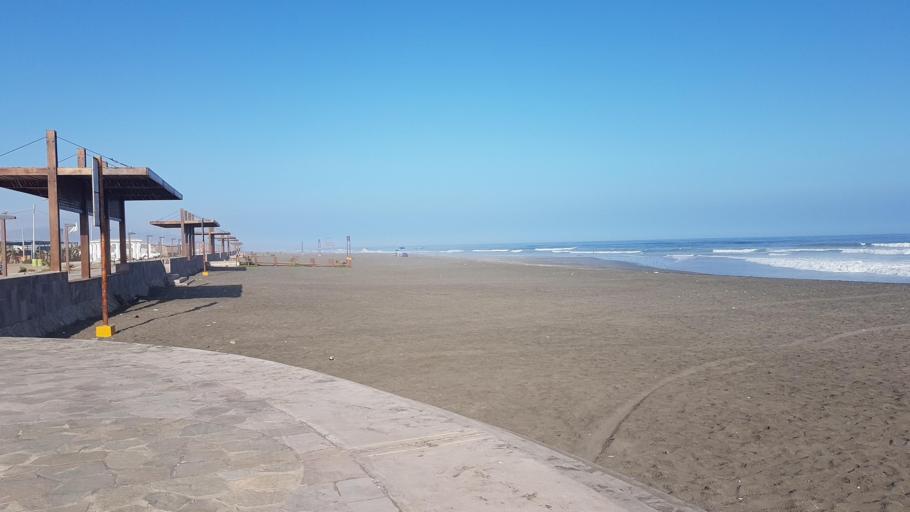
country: PE
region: Arequipa
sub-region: Provincia de Islay
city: Punta de Bombon
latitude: -17.1906
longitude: -71.7911
